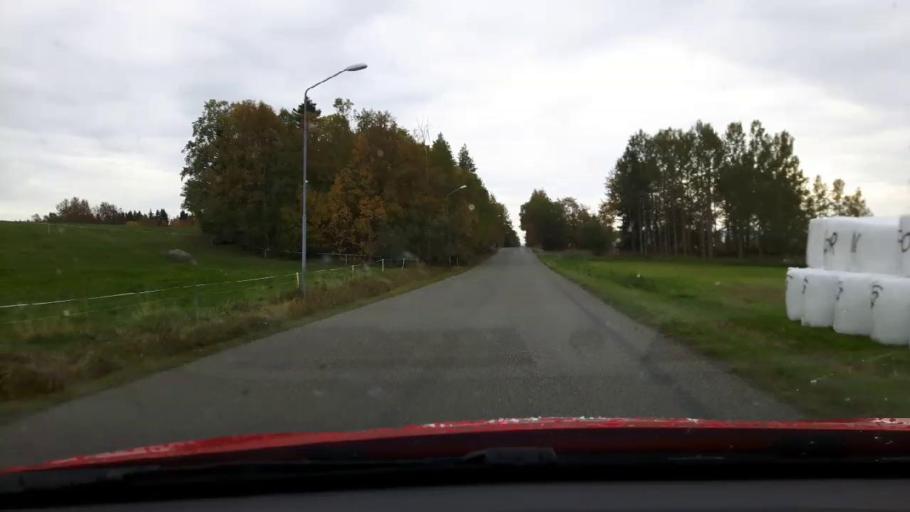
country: SE
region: Jaemtland
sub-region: Bergs Kommun
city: Hoverberg
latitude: 62.9545
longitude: 14.4905
